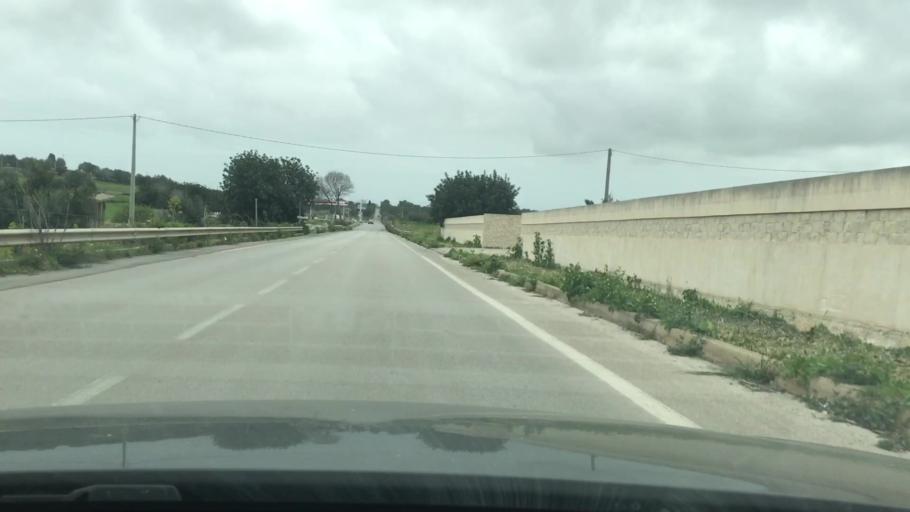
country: IT
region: Sicily
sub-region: Ragusa
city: Scicli
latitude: 36.8150
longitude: 14.7338
